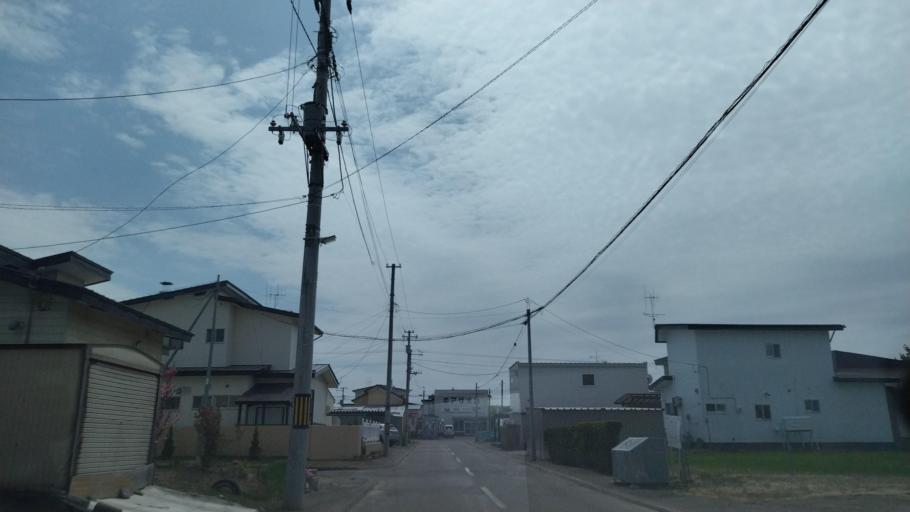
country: JP
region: Hokkaido
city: Otofuke
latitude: 43.2414
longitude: 143.5537
